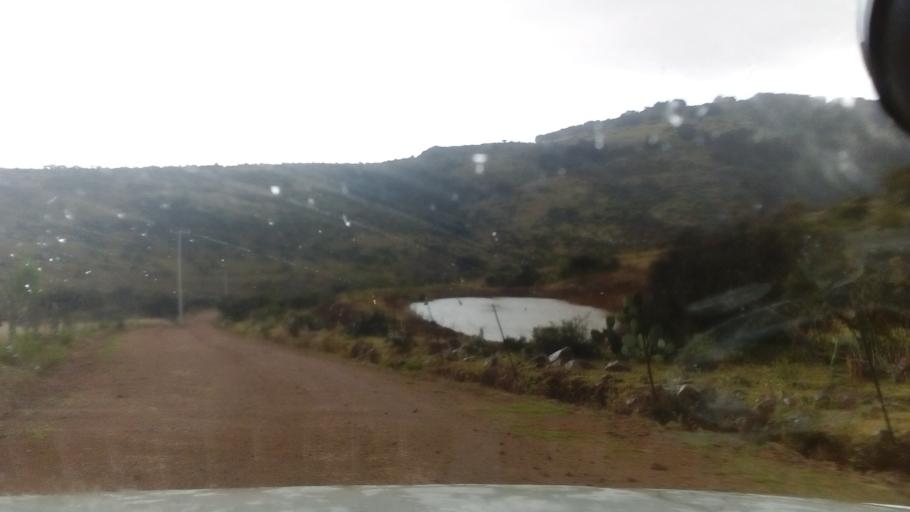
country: MX
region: Guanajuato
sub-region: Silao de la Victoria
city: San Francisco (Banos de Agua Caliente)
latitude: 21.1581
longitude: -101.4364
